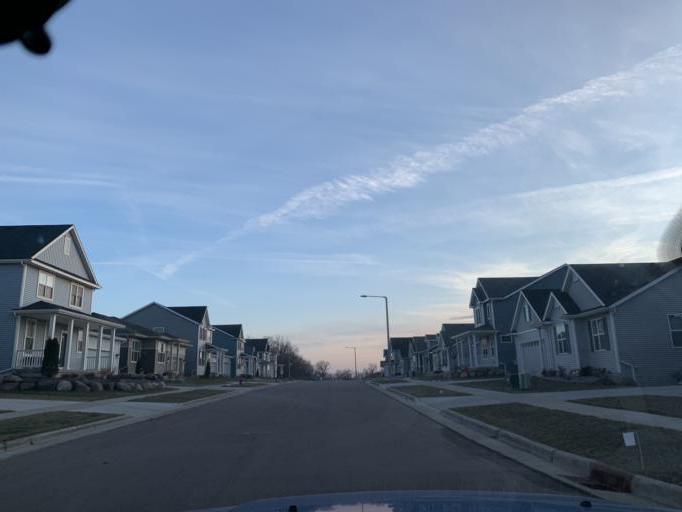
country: US
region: Wisconsin
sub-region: Dane County
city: Verona
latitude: 43.0566
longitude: -89.5662
